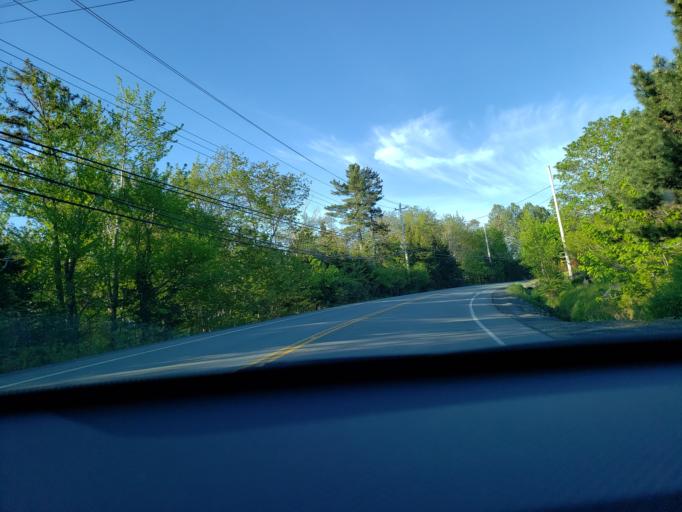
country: CA
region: Nova Scotia
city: Cole Harbour
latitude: 44.7254
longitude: -63.3949
